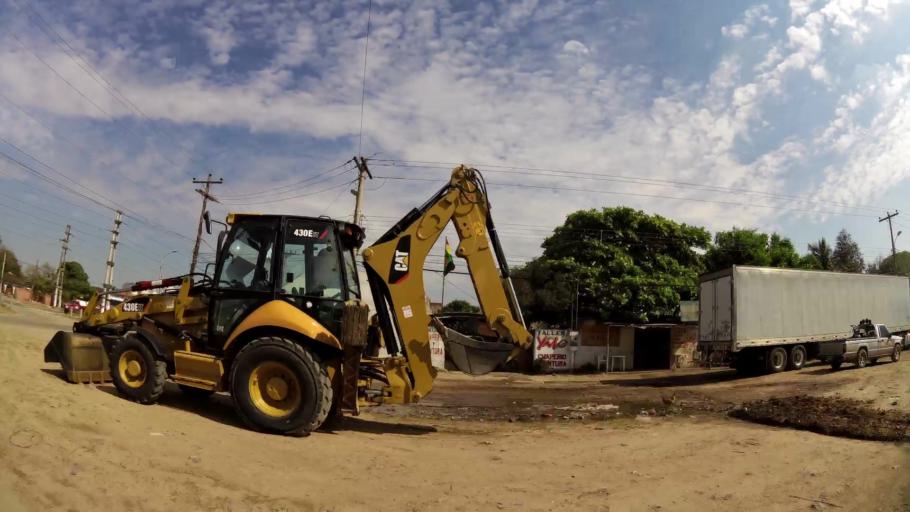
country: BO
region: Santa Cruz
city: Santa Cruz de la Sierra
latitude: -17.7276
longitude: -63.1584
